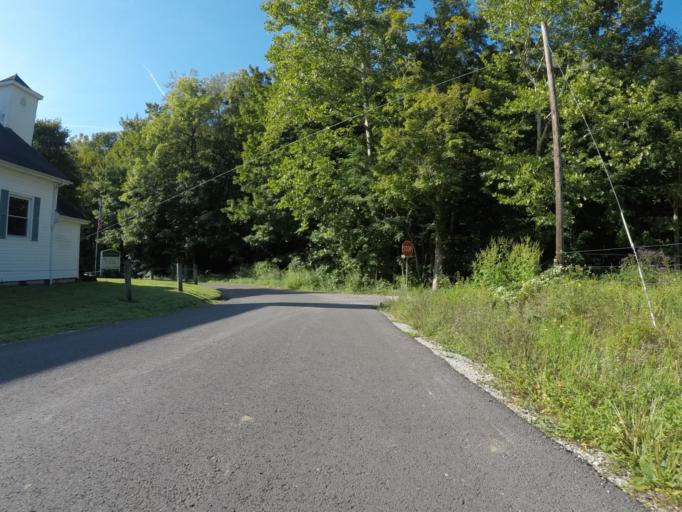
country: US
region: Ohio
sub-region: Lawrence County
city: Burlington
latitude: 38.5093
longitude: -82.5228
